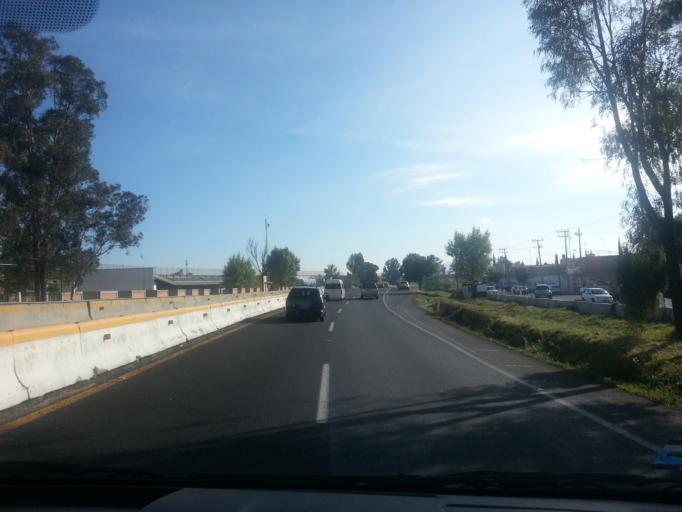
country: MX
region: Mexico
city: Ecatepec
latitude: 19.6080
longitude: -99.0349
